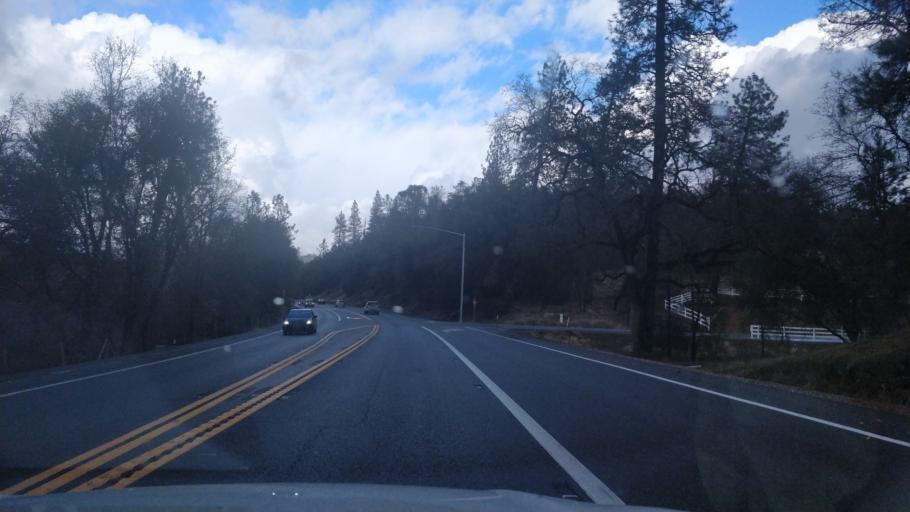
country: US
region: California
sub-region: Nevada County
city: Lake of the Pines
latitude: 39.0583
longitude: -121.0904
